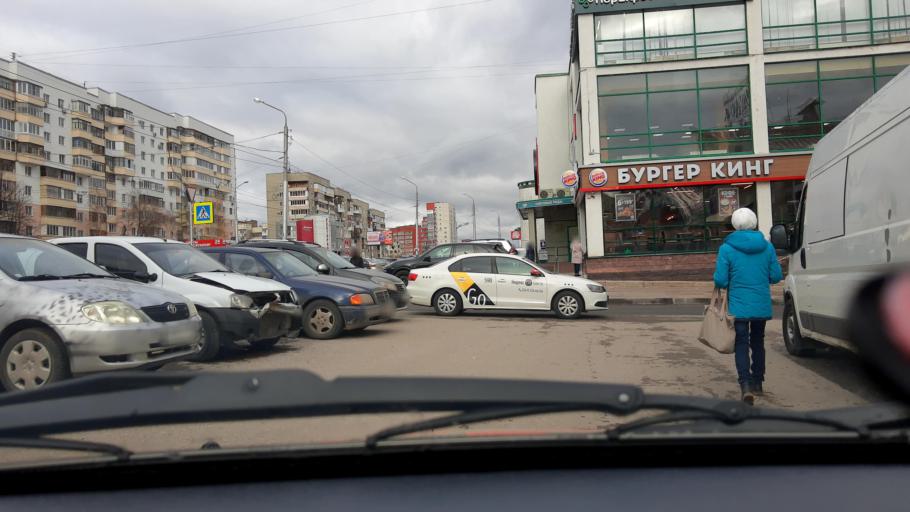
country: RU
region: Bashkortostan
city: Ufa
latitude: 54.7066
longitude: 55.9990
